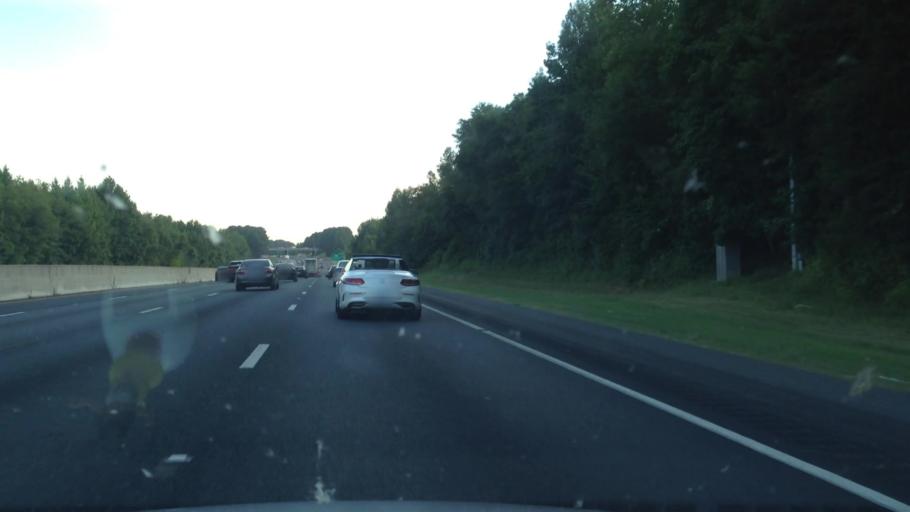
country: US
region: South Carolina
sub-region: York County
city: Fort Mill
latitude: 35.0679
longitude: -80.9515
